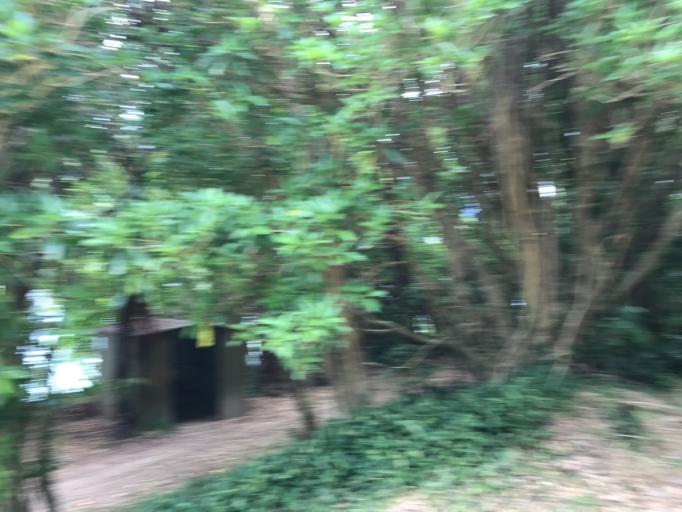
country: NZ
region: Marlborough
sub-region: Marlborough District
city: Picton
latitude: -41.1033
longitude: 174.1841
